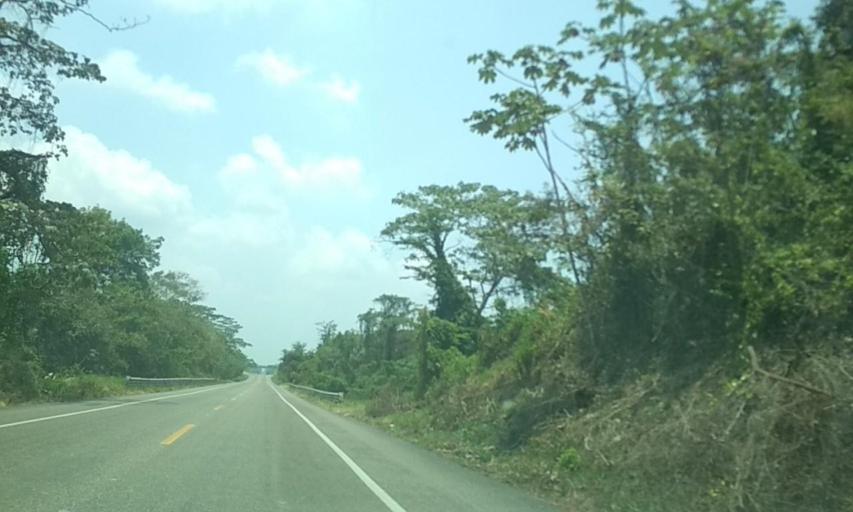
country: MX
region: Tabasco
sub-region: Huimanguillo
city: Francisco Rueda
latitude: 17.6657
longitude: -93.8618
